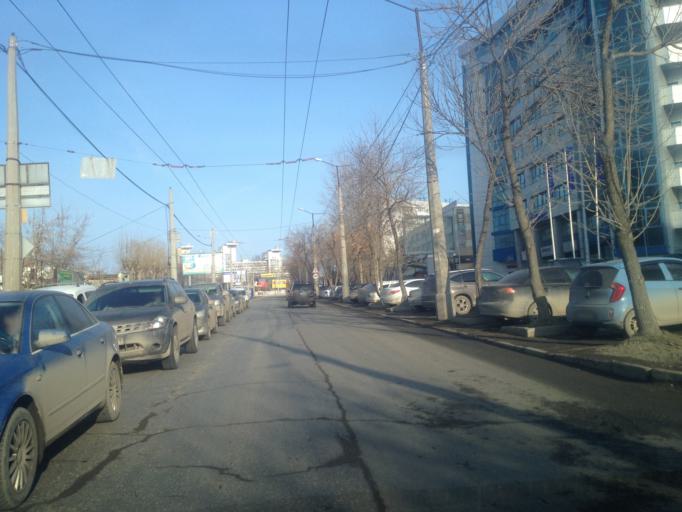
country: RU
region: Sverdlovsk
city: Yekaterinburg
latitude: 56.8231
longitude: 60.5702
